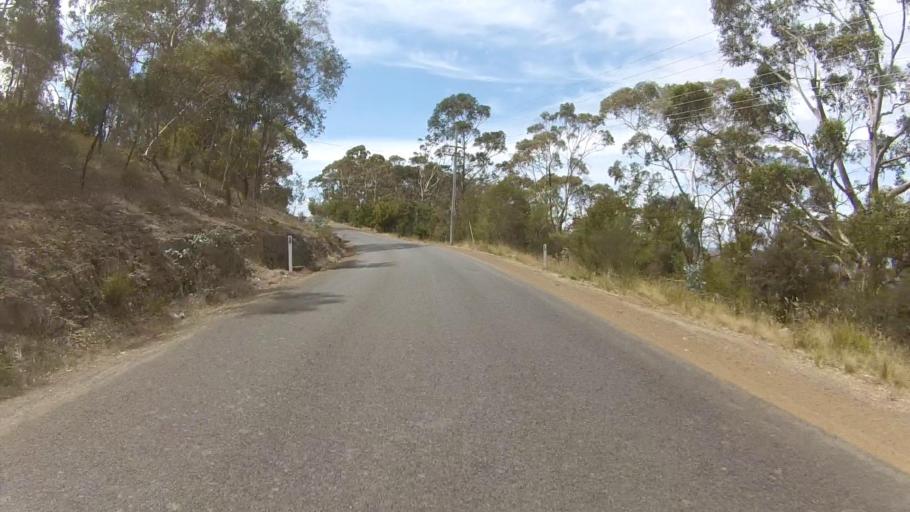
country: AU
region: Tasmania
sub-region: Kingborough
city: Blackmans Bay
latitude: -43.0524
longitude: 147.3391
